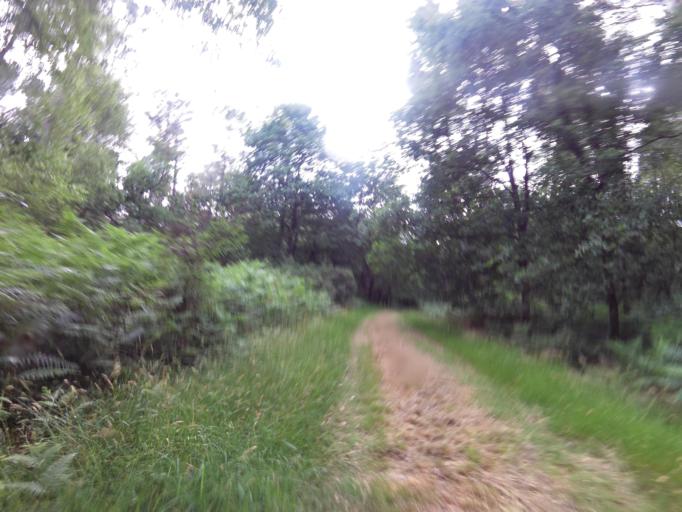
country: FR
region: Brittany
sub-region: Departement du Morbihan
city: Molac
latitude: 47.7618
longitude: -2.4160
